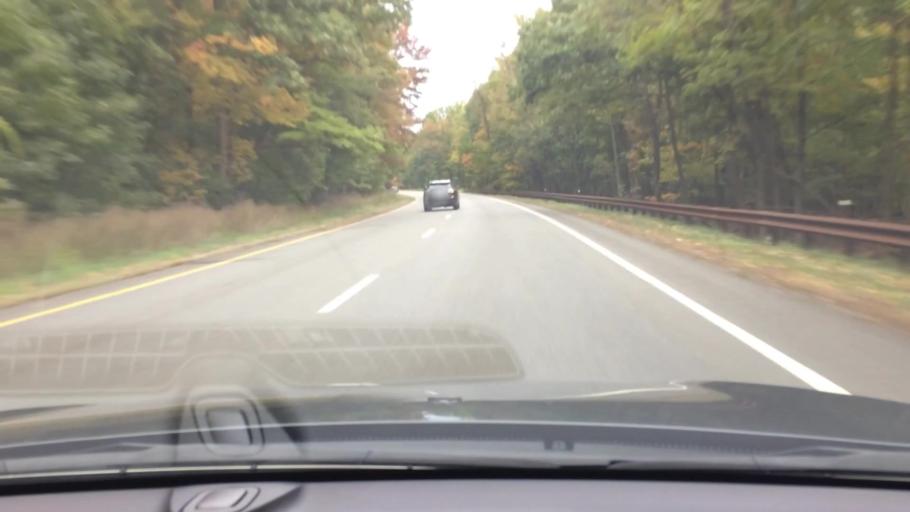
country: US
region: New Jersey
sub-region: Bergen County
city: Alpine
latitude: 40.9683
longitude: -73.9138
